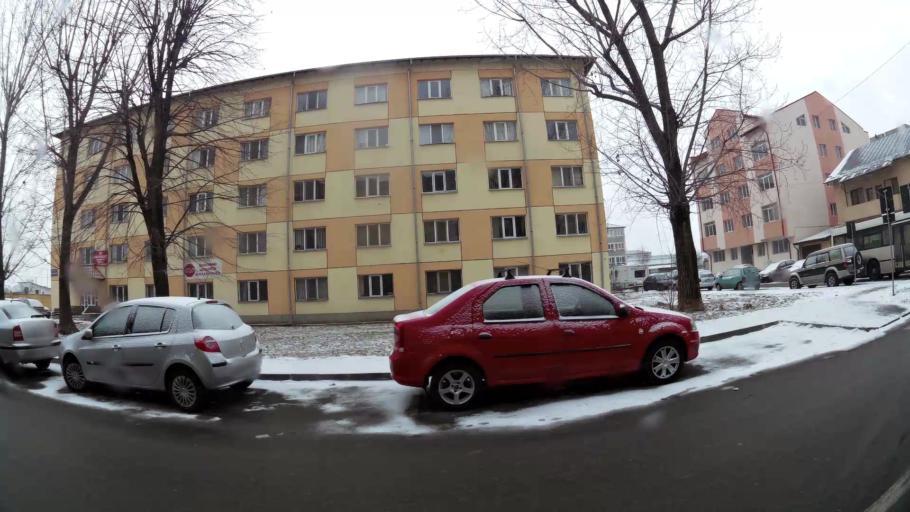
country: RO
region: Dambovita
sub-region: Municipiul Targoviste
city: Targoviste
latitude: 44.9154
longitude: 25.4698
